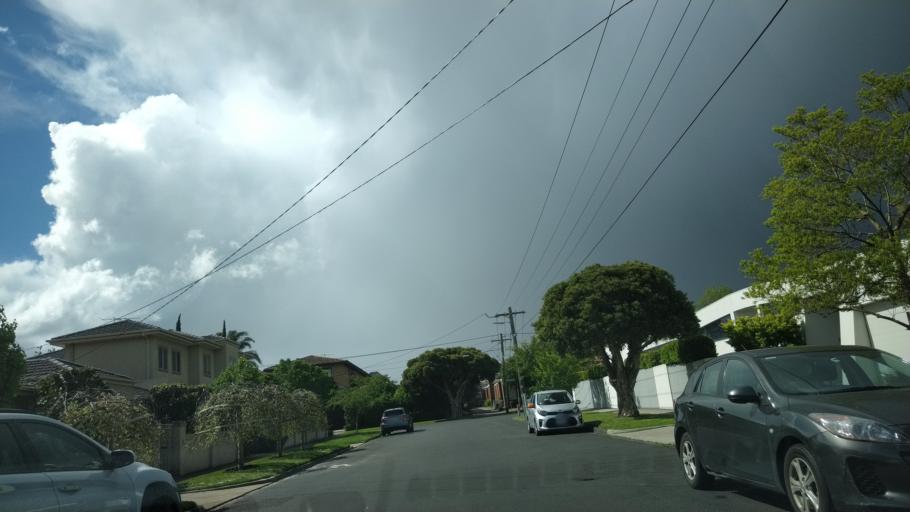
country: AU
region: Victoria
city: Caulfield North
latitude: -37.8787
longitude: 145.0271
